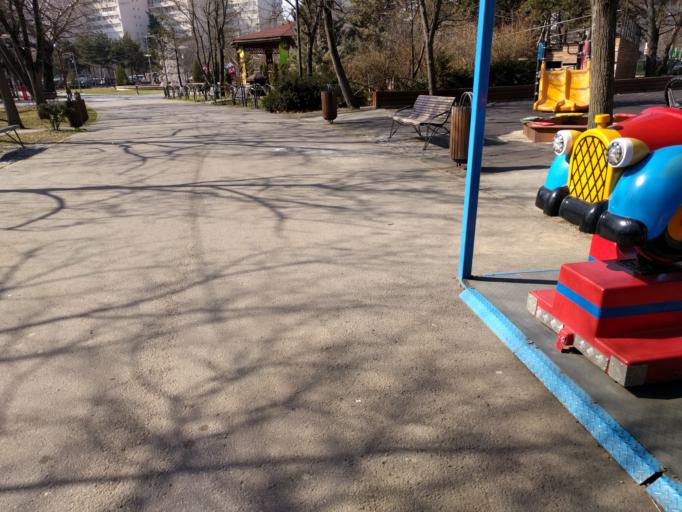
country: RO
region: Ilfov
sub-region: Comuna Fundeni-Dobroesti
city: Fundeni
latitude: 44.4260
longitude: 26.1516
